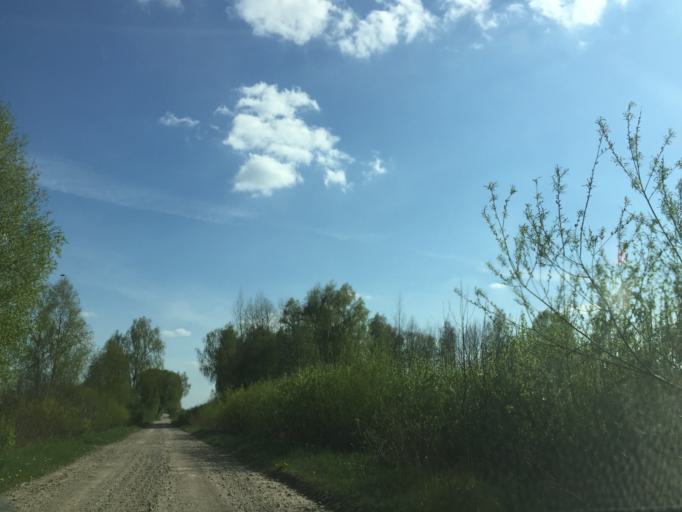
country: LV
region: Lecava
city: Iecava
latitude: 56.5057
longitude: 24.3180
